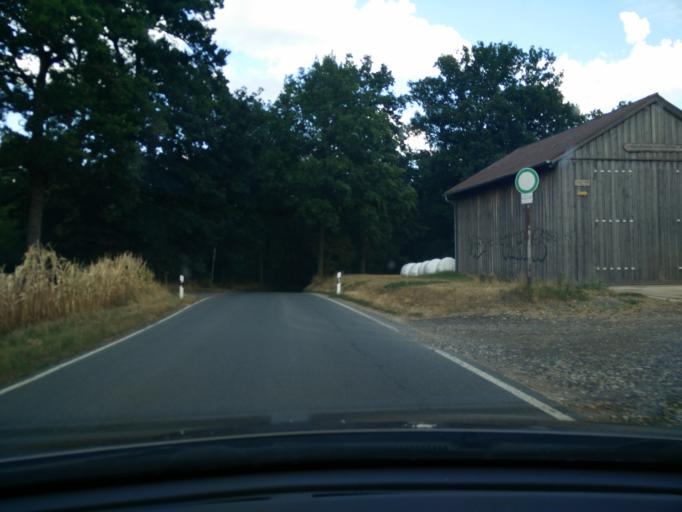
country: DE
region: Bavaria
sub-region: Regierungsbezirk Mittelfranken
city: Stein
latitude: 49.3871
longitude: 11.0197
